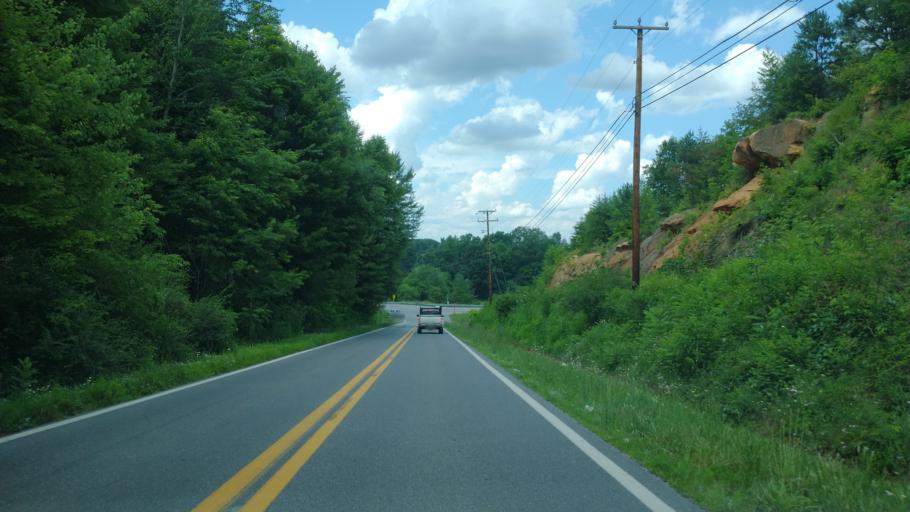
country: US
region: West Virginia
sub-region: Mercer County
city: Athens
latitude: 37.4236
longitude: -81.0639
